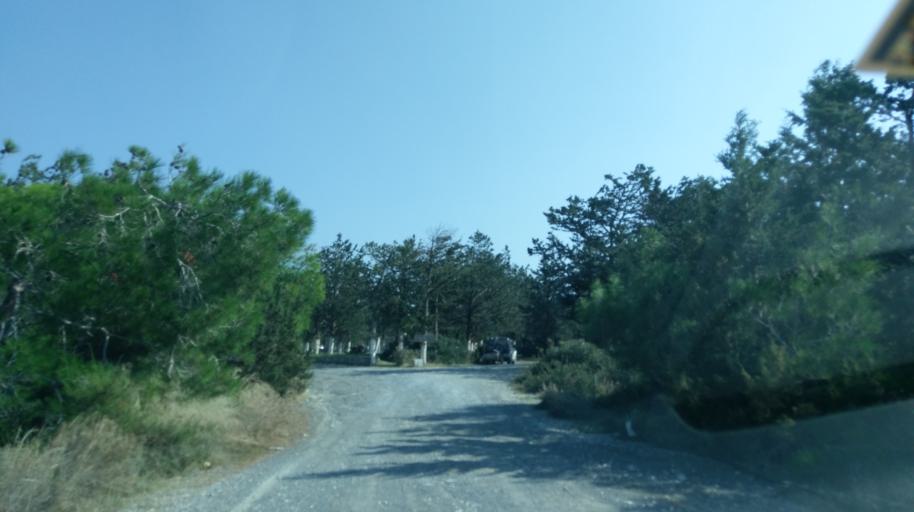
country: CY
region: Ammochostos
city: Lefkonoiko
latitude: 35.3416
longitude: 33.7224
